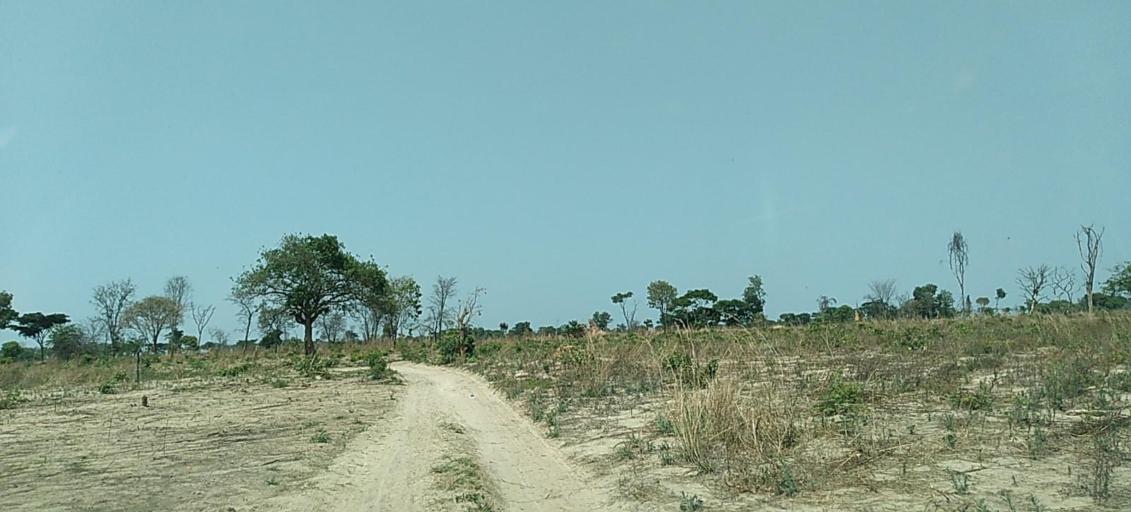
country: ZM
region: Copperbelt
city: Mpongwe
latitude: -13.8635
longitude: 28.0543
